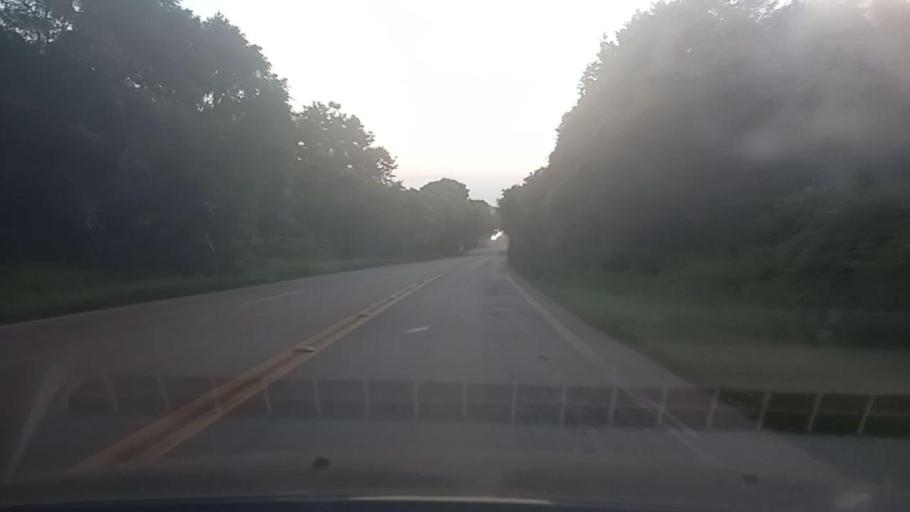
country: BR
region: Rio Grande do Sul
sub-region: Passo Fundo
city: Passo Fundo
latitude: -28.2913
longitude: -52.4563
